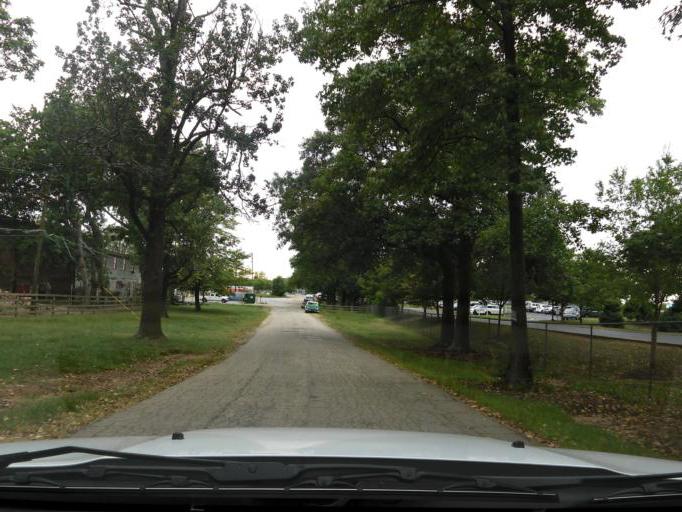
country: US
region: Georgia
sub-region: Fulton County
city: Atlanta
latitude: 33.7867
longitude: -84.4152
